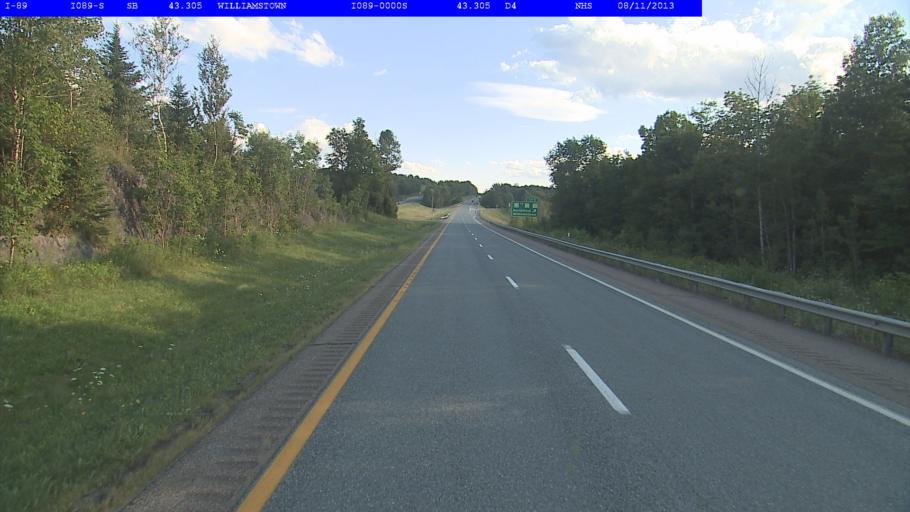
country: US
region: Vermont
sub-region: Washington County
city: Northfield
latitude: 44.1200
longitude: -72.6056
